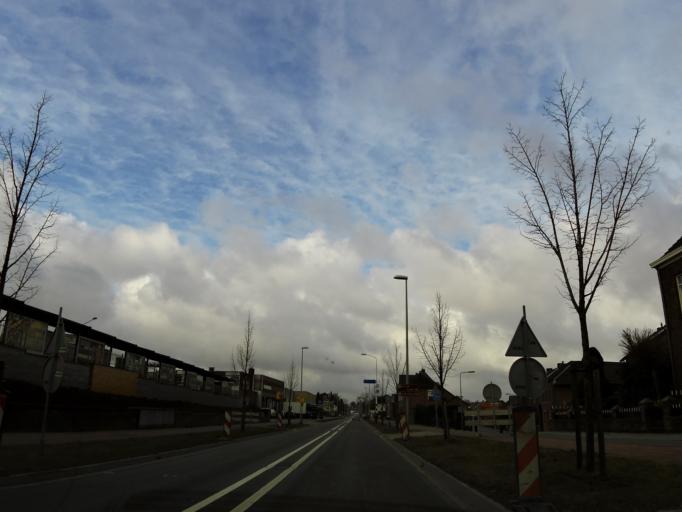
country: NL
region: Limburg
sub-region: Eijsden-Margraten
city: Margraten
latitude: 50.8170
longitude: 5.8330
